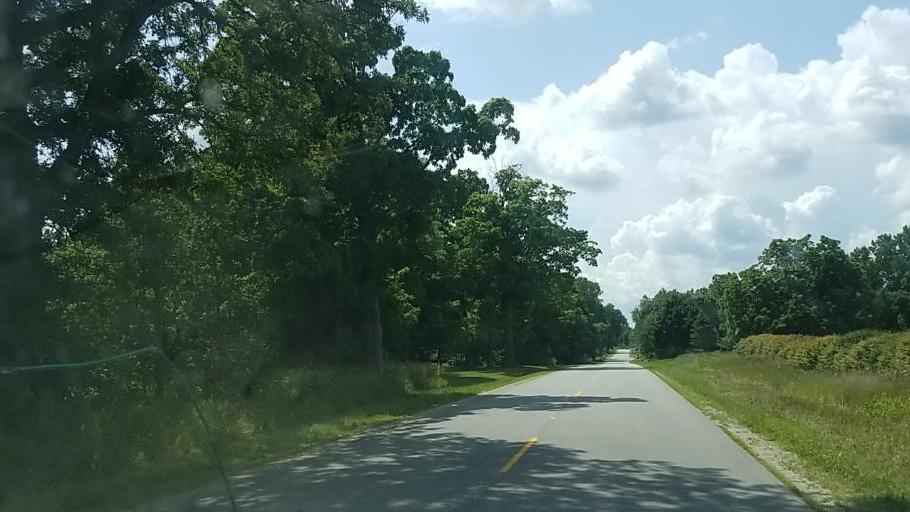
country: US
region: Michigan
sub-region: Muskegon County
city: Ravenna
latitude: 43.1967
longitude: -85.8794
